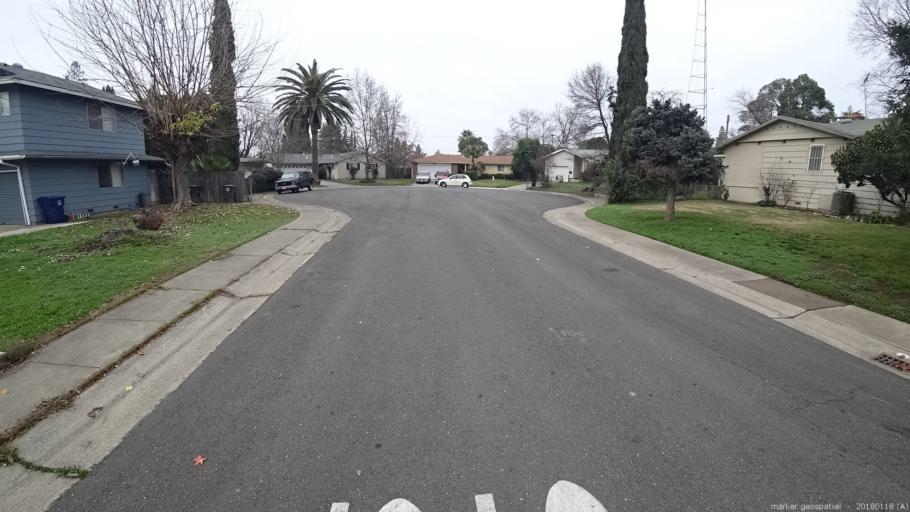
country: US
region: California
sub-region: Sacramento County
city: Rancho Cordova
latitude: 38.5884
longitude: -121.3136
